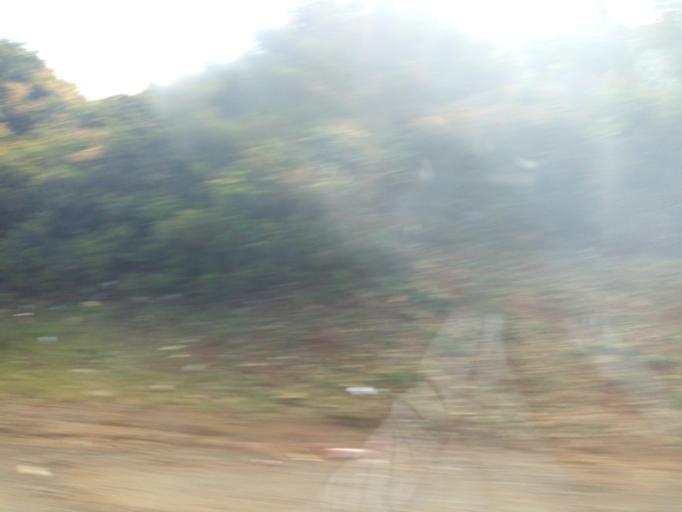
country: KE
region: Nakuru
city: Kijabe
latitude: -1.0178
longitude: 36.6019
